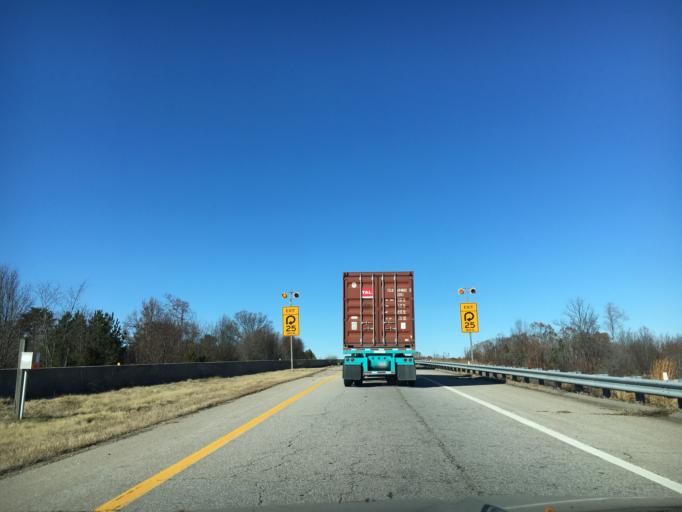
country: US
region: Virginia
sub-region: Pittsylvania County
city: Mount Hermon
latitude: 36.6034
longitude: -79.5365
